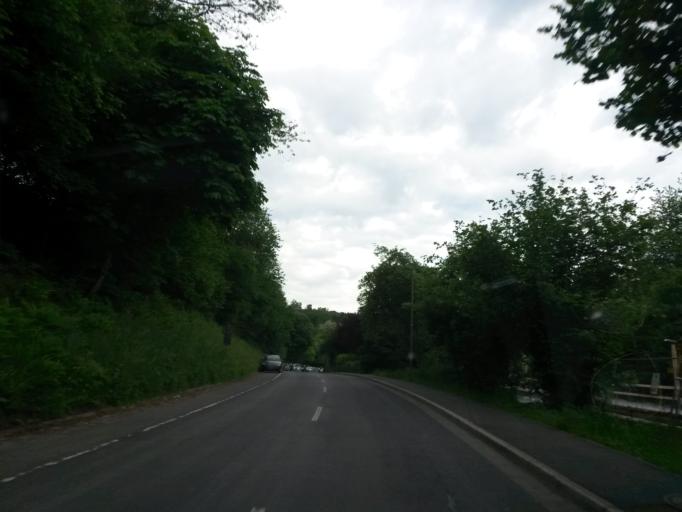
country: DE
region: North Rhine-Westphalia
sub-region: Regierungsbezirk Koln
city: Overath
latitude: 50.9105
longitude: 7.2545
